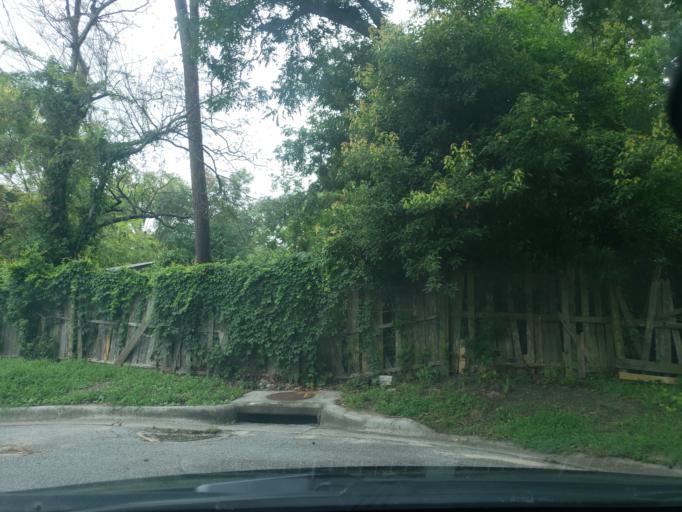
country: US
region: Georgia
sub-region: Chatham County
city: Montgomery
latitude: 31.9937
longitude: -81.1237
